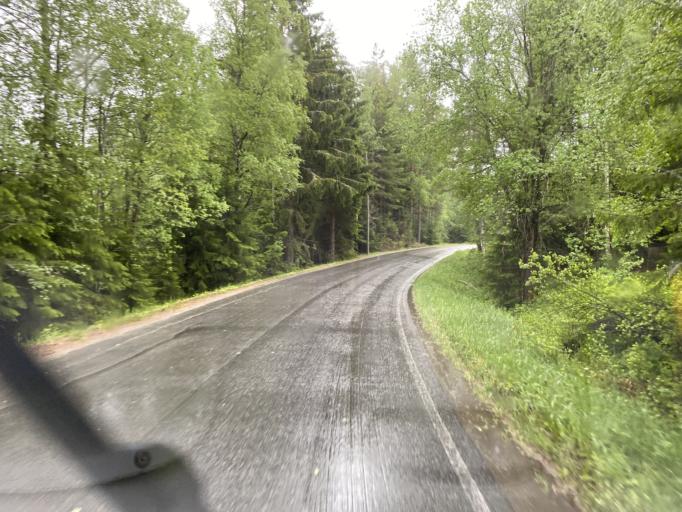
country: FI
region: Haeme
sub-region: Forssa
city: Humppila
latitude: 61.0752
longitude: 23.3113
